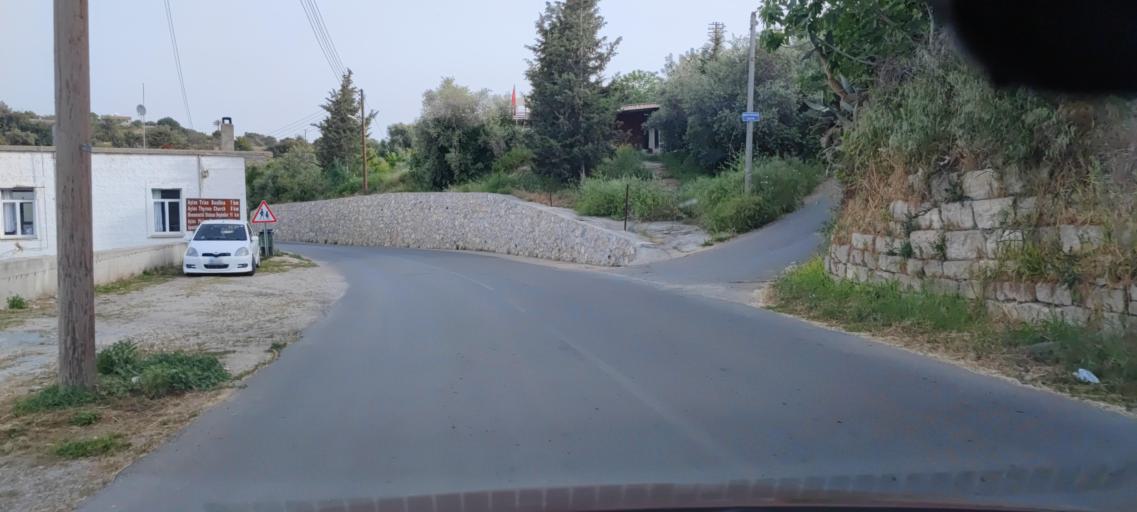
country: CY
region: Ammochostos
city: Leonarisso
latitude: 35.5364
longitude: 34.1916
